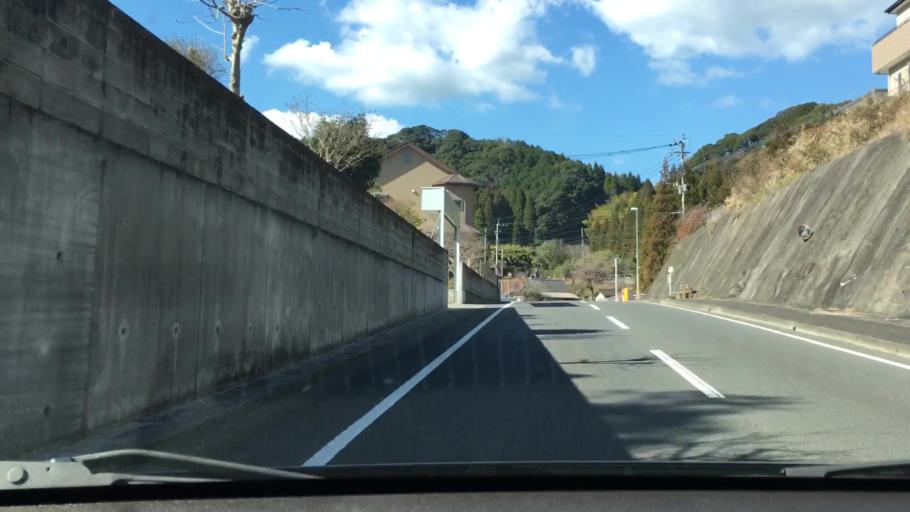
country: JP
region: Kagoshima
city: Ijuin
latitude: 31.6996
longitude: 130.4582
